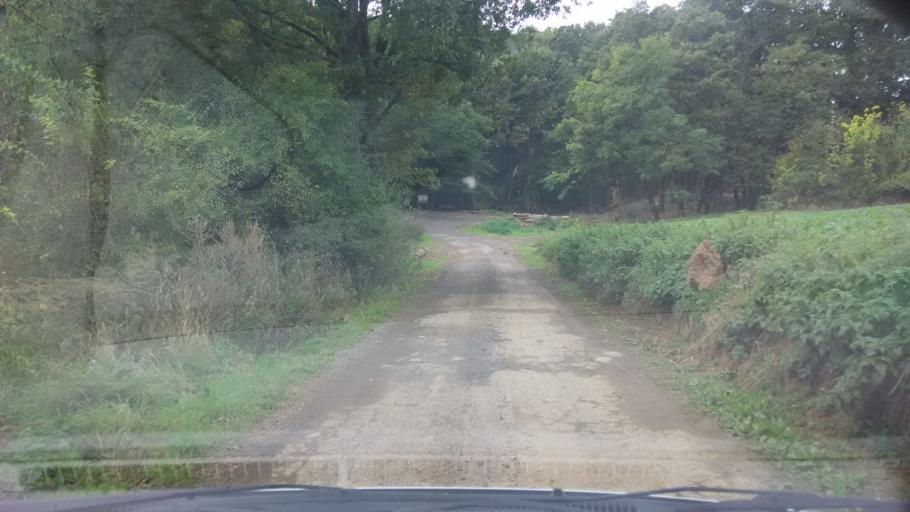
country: SK
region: Nitriansky
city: Tlmace
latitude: 48.2985
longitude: 18.4960
